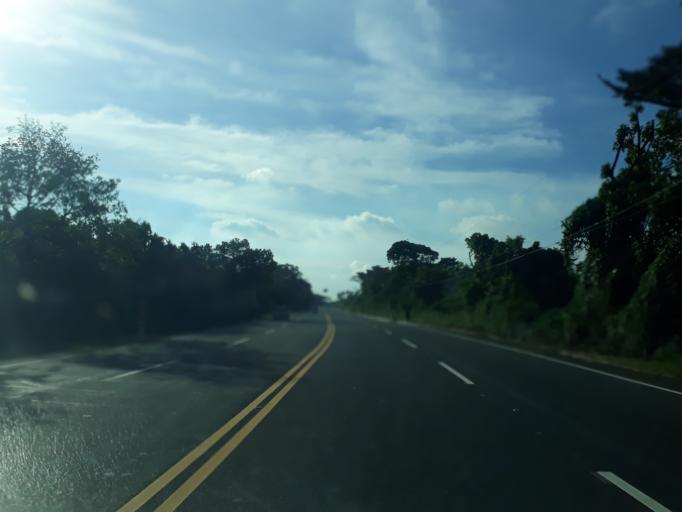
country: NI
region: Carazo
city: Diriamba
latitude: 11.9154
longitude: -86.2713
